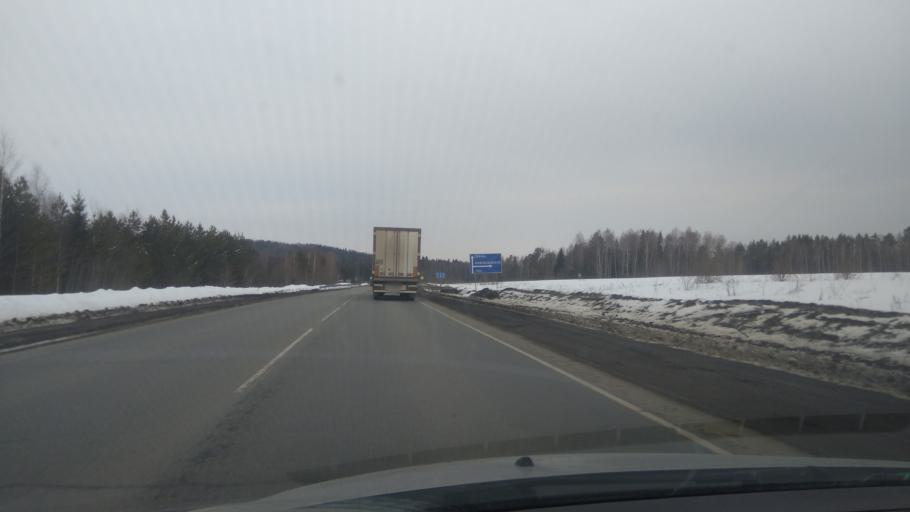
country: RU
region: Sverdlovsk
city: Ufimskiy
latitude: 56.7823
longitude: 58.2802
